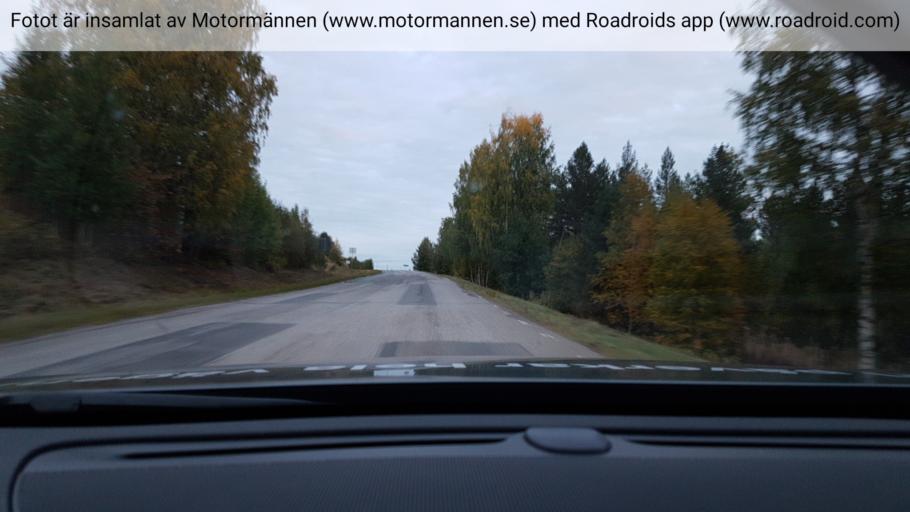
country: SE
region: Norrbotten
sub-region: Alvsbyns Kommun
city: AElvsbyn
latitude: 65.8551
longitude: 20.4319
